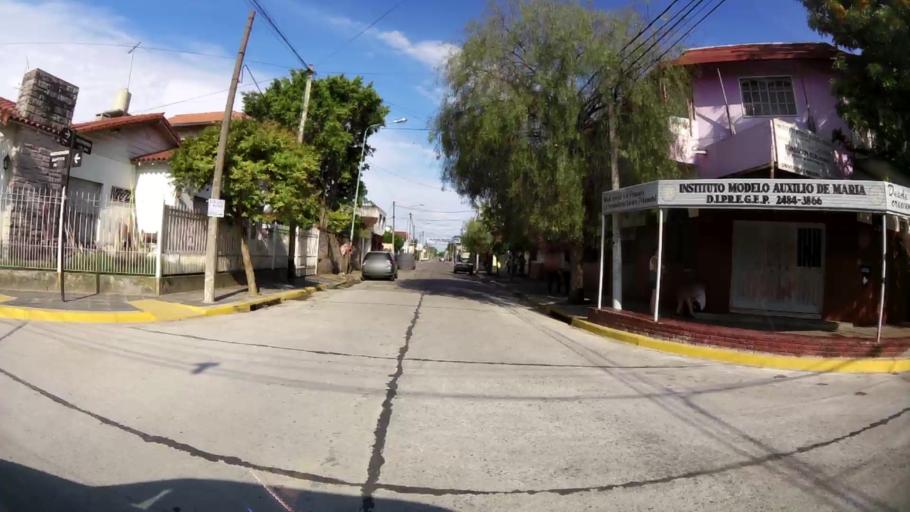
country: AR
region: Buenos Aires
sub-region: Partido de Merlo
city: Merlo
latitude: -34.6613
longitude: -58.7241
